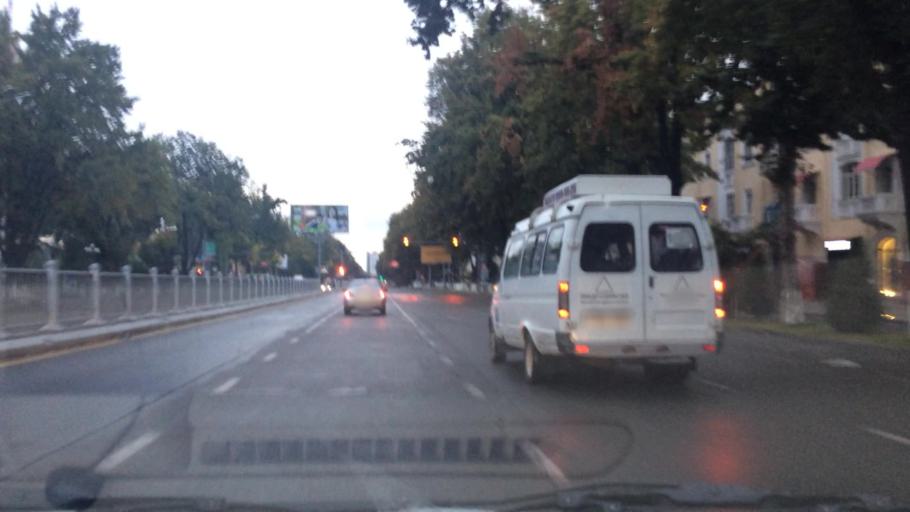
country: UZ
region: Toshkent Shahri
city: Tashkent
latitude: 41.3207
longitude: 69.2624
